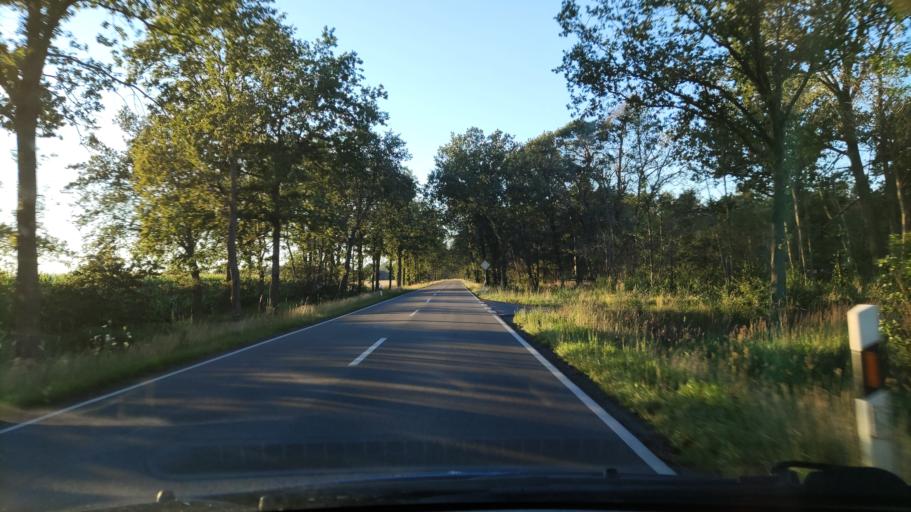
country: DE
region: Lower Saxony
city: Klein Gusborn
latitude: 53.0423
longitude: 11.1777
